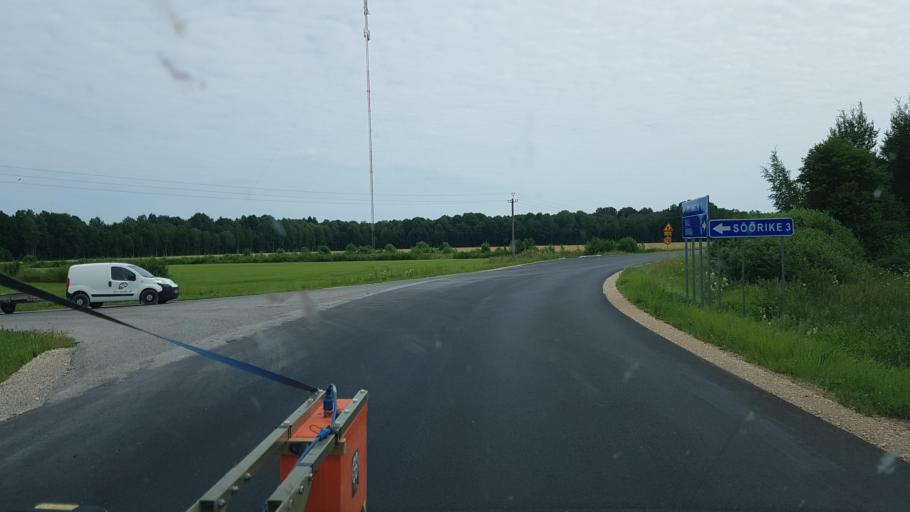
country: EE
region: Paernumaa
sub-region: Halinga vald
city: Parnu-Jaagupi
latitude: 58.6236
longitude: 24.3650
